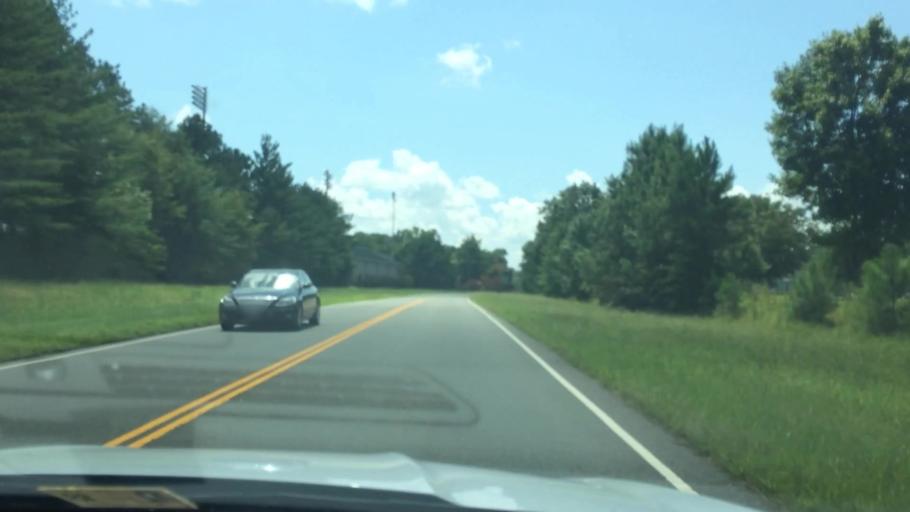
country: US
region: Virginia
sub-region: James City County
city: Williamsburg
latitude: 37.2923
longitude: -76.7342
